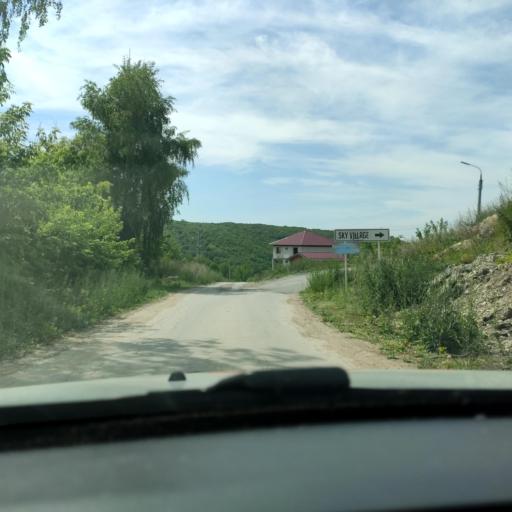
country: RU
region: Samara
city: Volzhskiy
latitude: 53.3400
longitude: 50.2002
